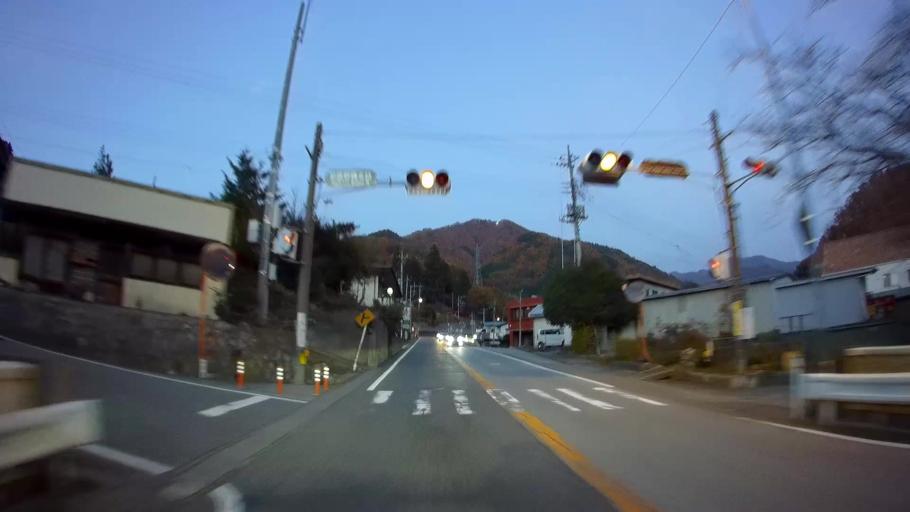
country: JP
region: Yamanashi
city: Enzan
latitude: 35.6393
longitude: 138.7826
